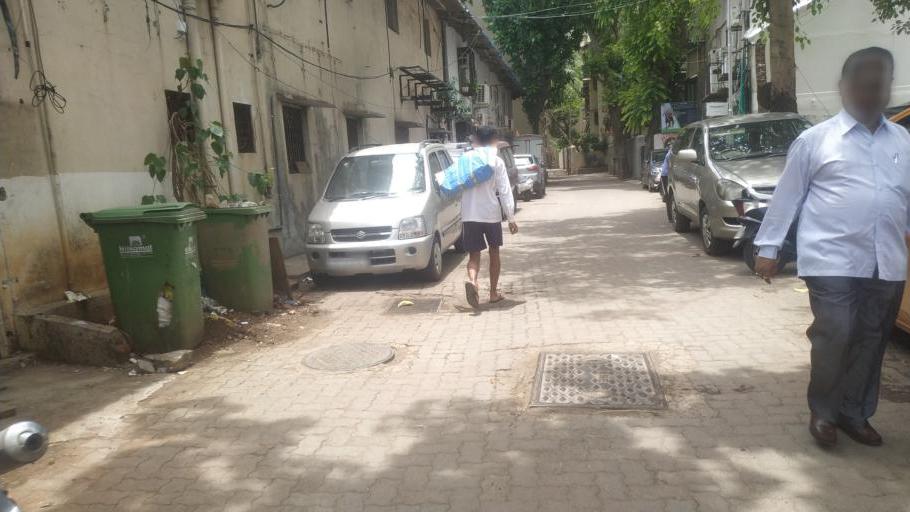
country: IN
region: Maharashtra
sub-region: Mumbai Suburban
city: Mumbai
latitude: 18.9929
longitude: 72.8378
